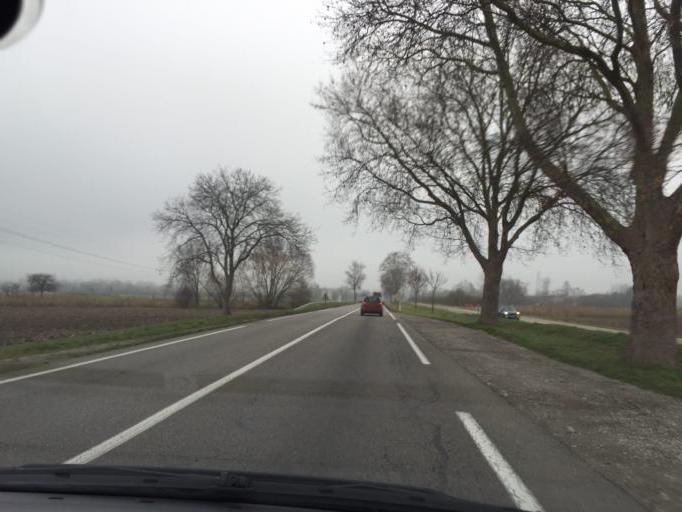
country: FR
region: Alsace
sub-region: Departement du Haut-Rhin
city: Algolsheim
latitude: 48.0117
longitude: 7.5559
